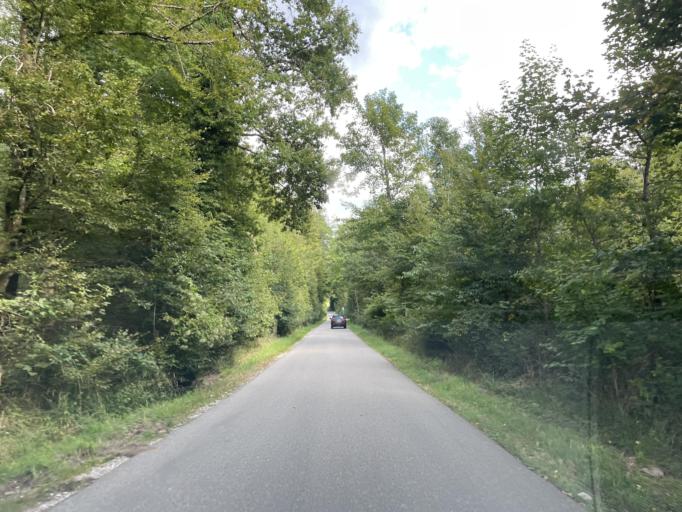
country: CH
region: Zurich
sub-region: Bezirk Winterthur
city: Mattenbach (Kreis 7)
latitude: 47.4761
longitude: 8.7353
